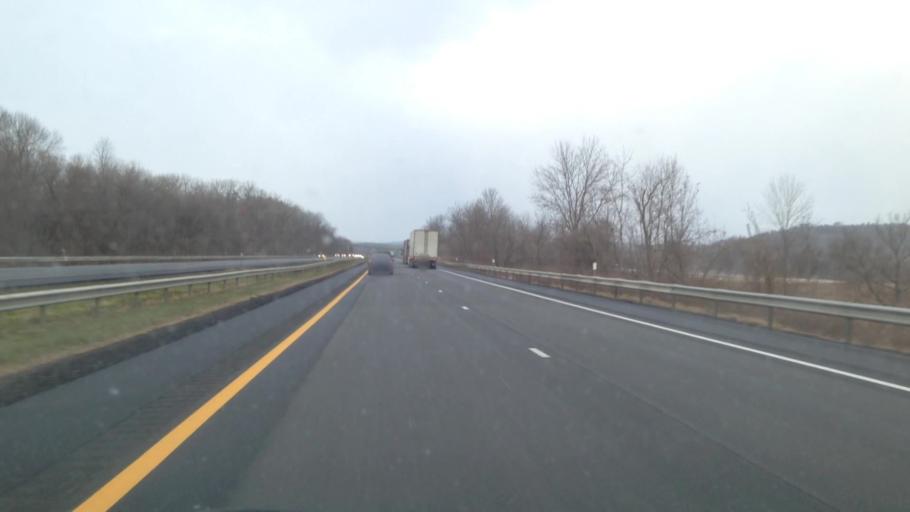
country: US
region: New York
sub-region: Montgomery County
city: Fonda
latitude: 42.9381
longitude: -74.3336
